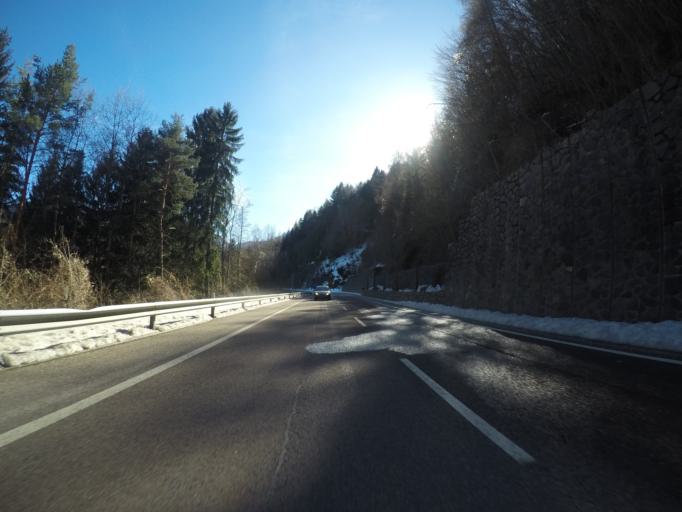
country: IT
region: Trentino-Alto Adige
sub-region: Provincia di Trento
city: Capriana
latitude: 46.2654
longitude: 11.3424
